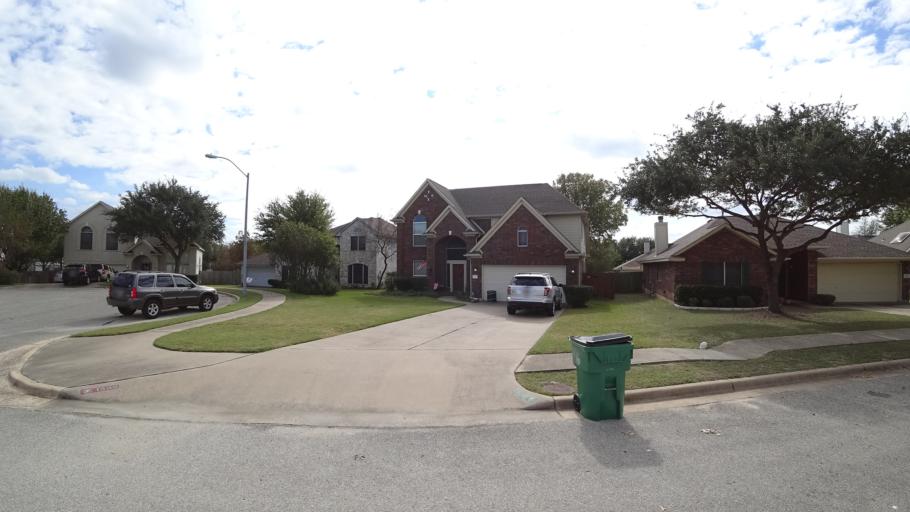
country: US
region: Texas
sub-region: Travis County
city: Pflugerville
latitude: 30.4387
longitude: -97.6416
